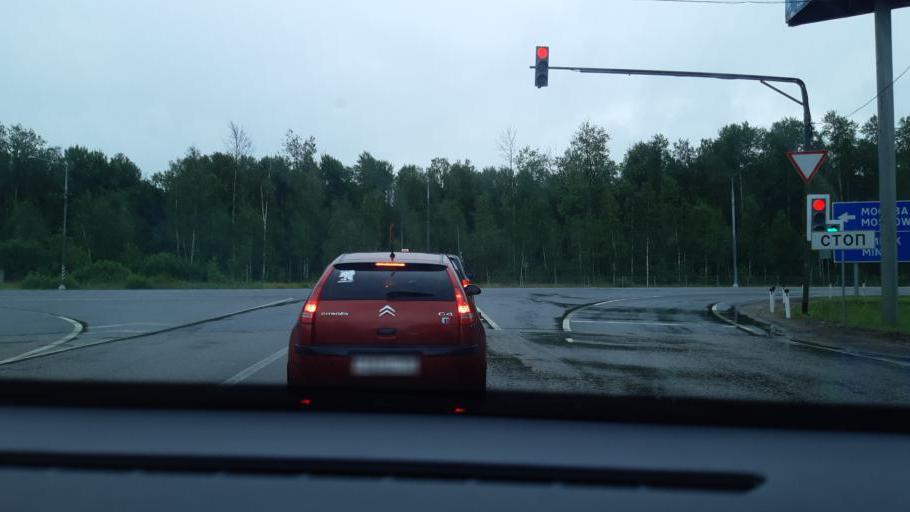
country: RU
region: Smolensk
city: Gagarin
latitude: 55.5000
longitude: 35.0363
